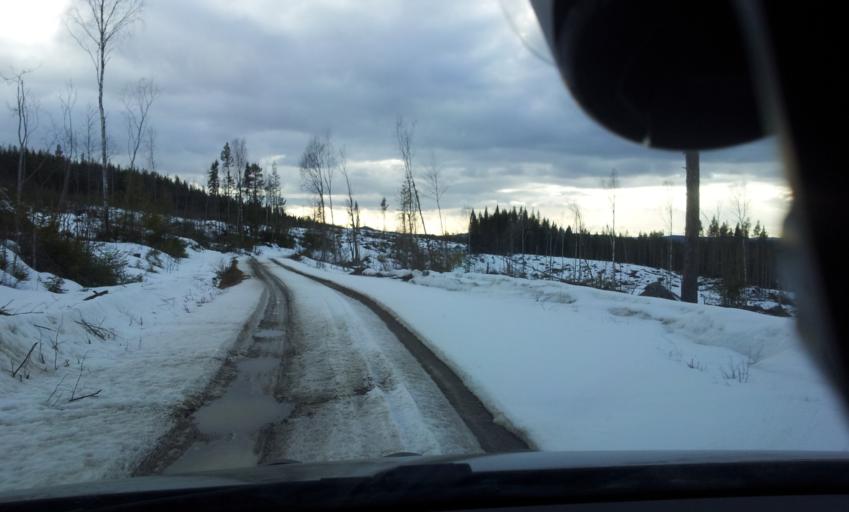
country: SE
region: Vaesternorrland
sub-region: Ange Kommun
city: Ange
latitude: 62.1922
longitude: 15.7251
